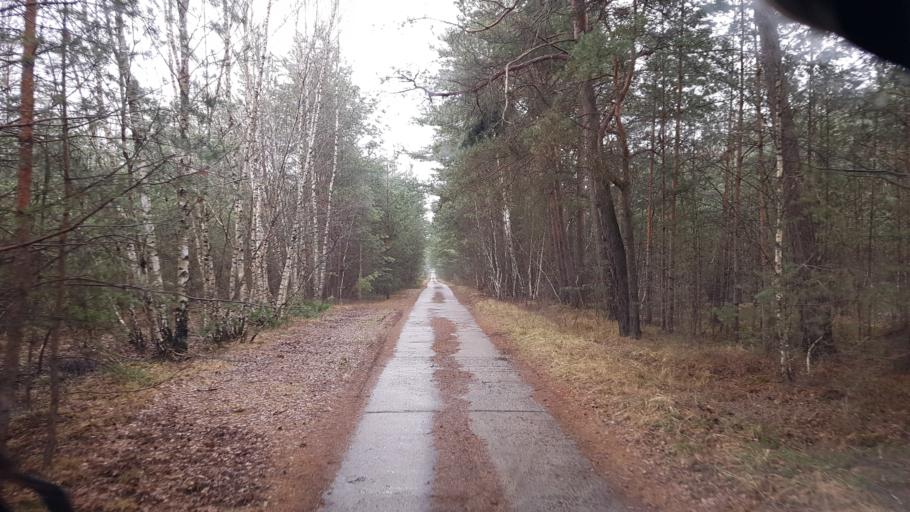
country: DE
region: Brandenburg
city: Grossraschen
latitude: 51.6088
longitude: 13.9867
